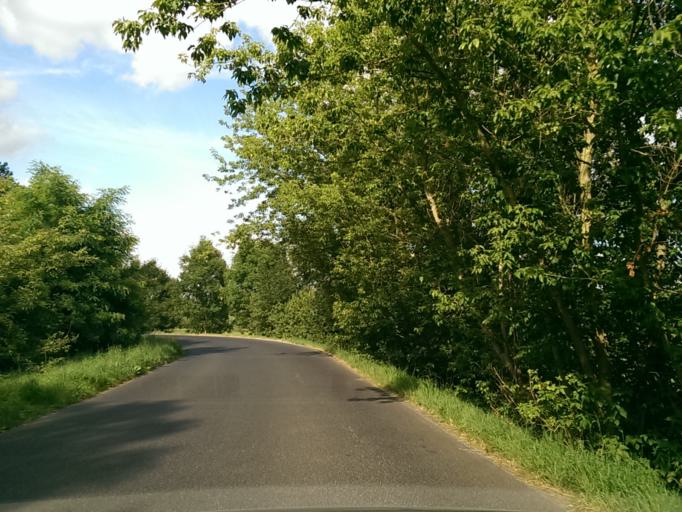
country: CZ
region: Central Bohemia
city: Bakov nad Jizerou
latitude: 50.4736
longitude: 14.9261
